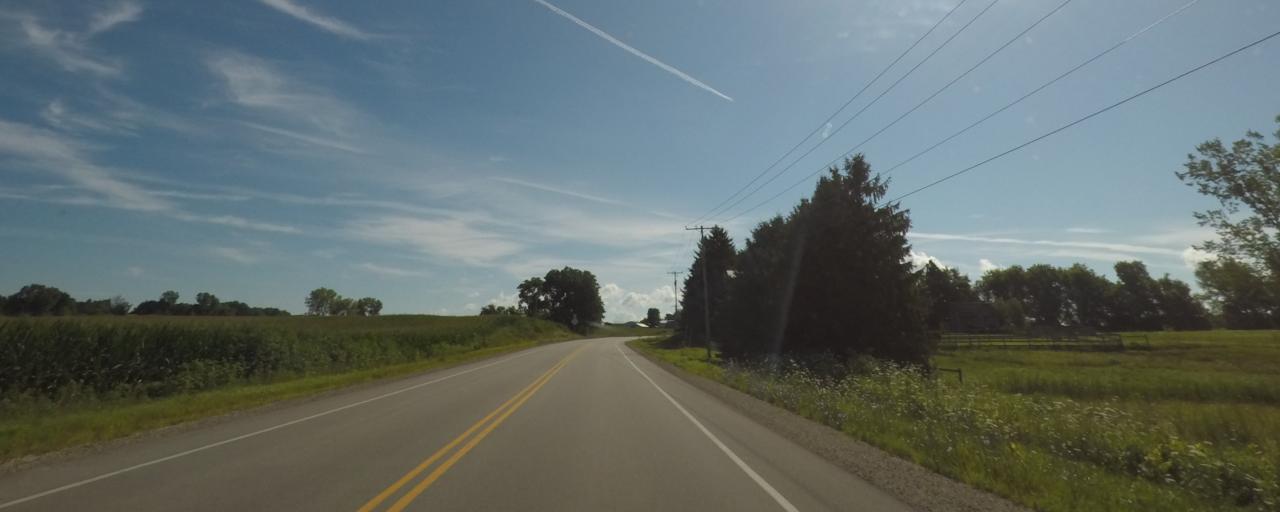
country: US
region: Wisconsin
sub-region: Jefferson County
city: Johnson Creek
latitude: 43.0748
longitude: -88.6796
